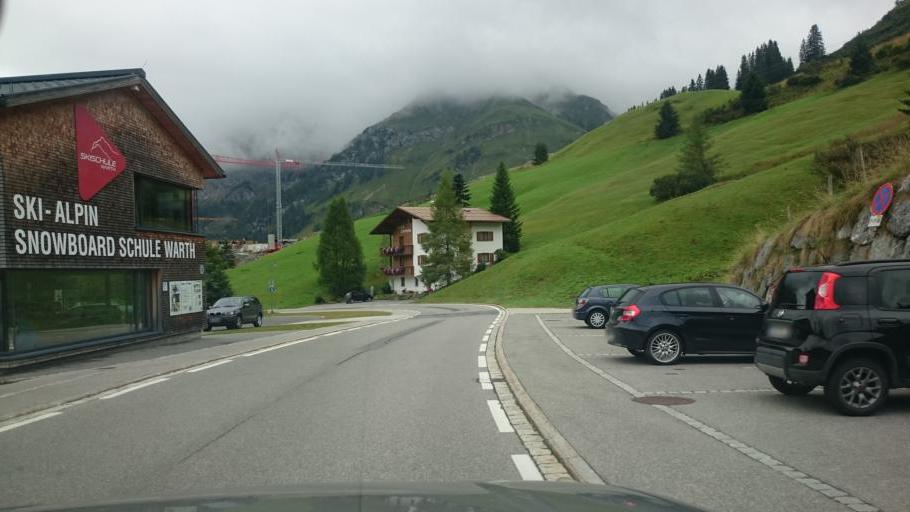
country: AT
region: Vorarlberg
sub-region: Politischer Bezirk Bregenz
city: Warth
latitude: 47.2598
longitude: 10.1771
